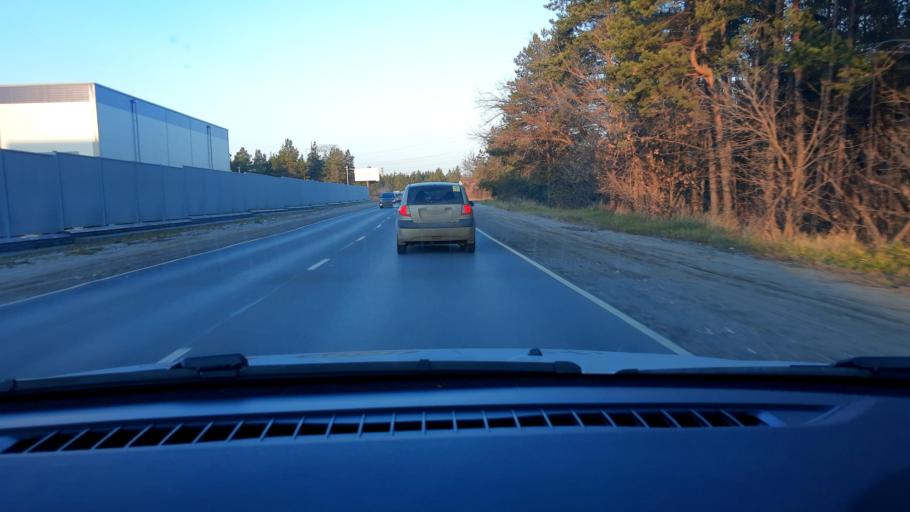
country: RU
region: Nizjnij Novgorod
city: Dzerzhinsk
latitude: 56.2585
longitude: 43.4632
